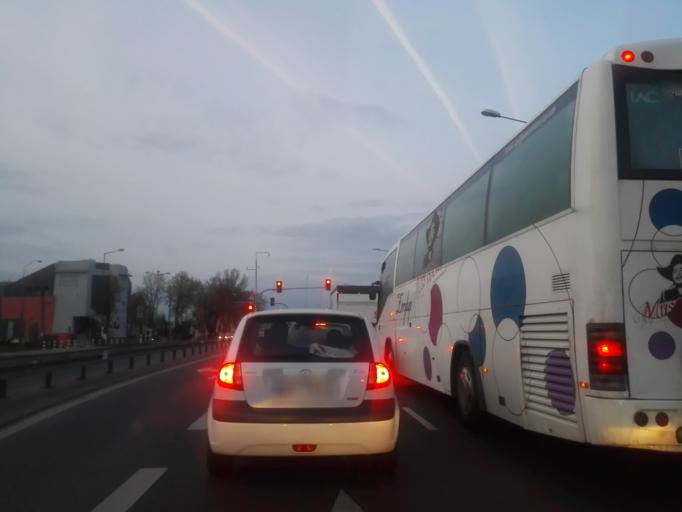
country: PL
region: Masovian Voivodeship
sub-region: Powiat pruszkowski
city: Raszyn
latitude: 52.1531
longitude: 20.9195
